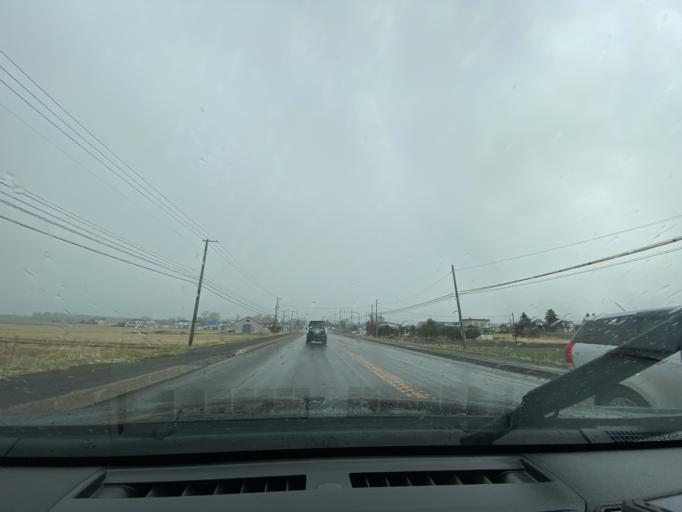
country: JP
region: Hokkaido
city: Takikawa
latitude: 43.6152
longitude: 141.9362
